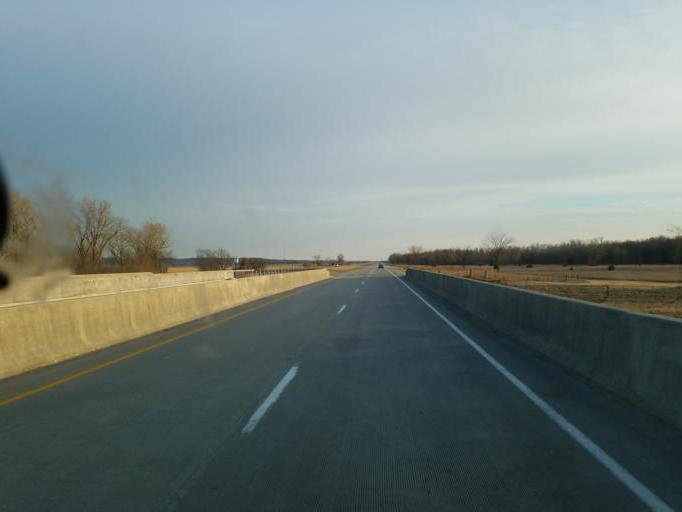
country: US
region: Nebraska
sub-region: Burt County
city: Tekamah
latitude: 41.8209
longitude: -96.0729
